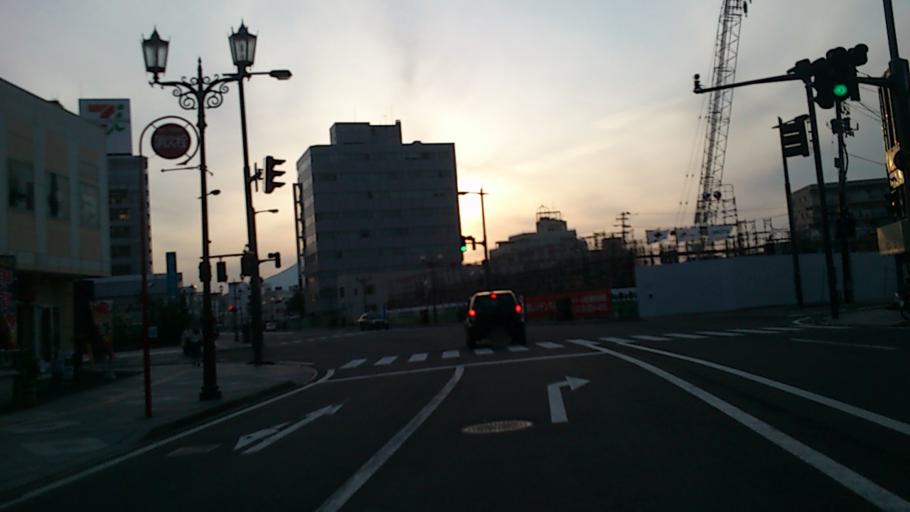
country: JP
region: Aomori
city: Hirosaki
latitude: 40.5996
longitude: 140.4833
